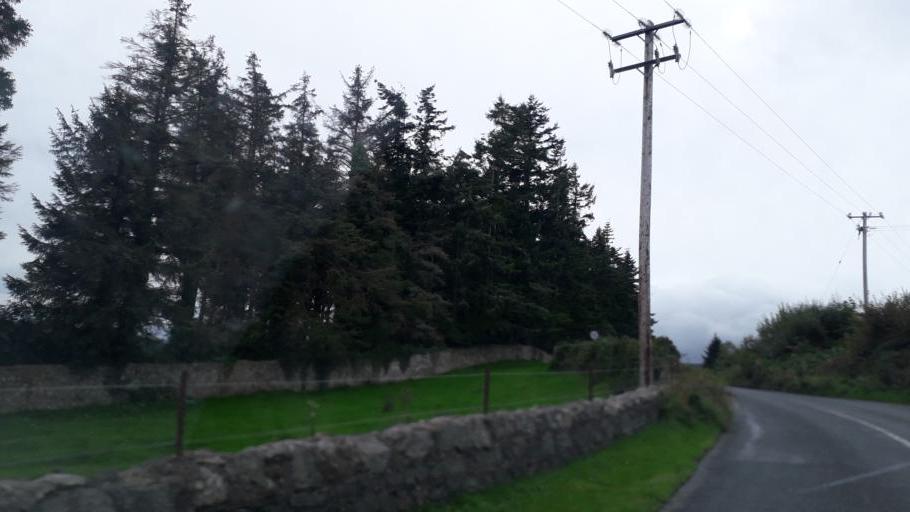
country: IE
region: Leinster
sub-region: Wicklow
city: Enniskerry
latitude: 53.1946
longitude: -6.1980
